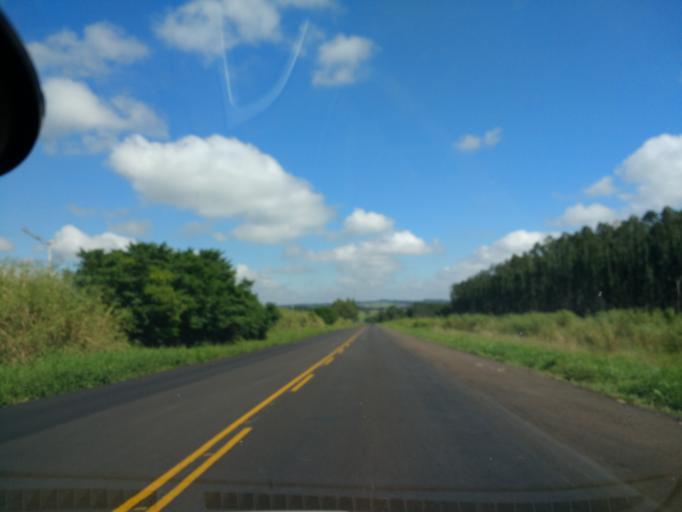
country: BR
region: Parana
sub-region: Cianorte
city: Cianorte
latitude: -23.7342
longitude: -52.7030
